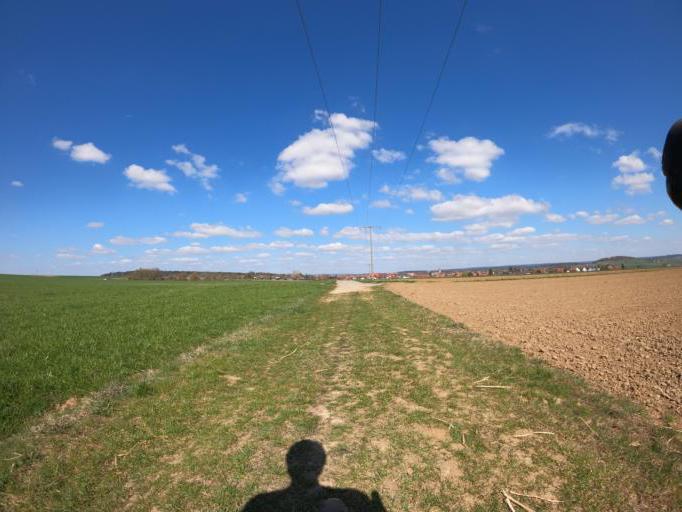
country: DE
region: Baden-Wuerttemberg
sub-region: Tuebingen Region
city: Rottenburg
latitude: 48.4742
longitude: 8.8847
